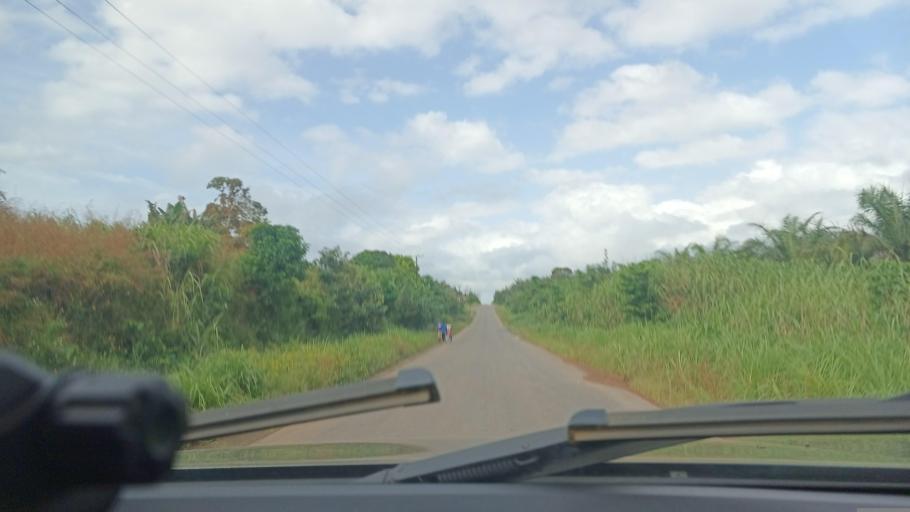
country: LR
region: Bomi
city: Tubmanburg
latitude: 6.7274
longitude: -11.0331
